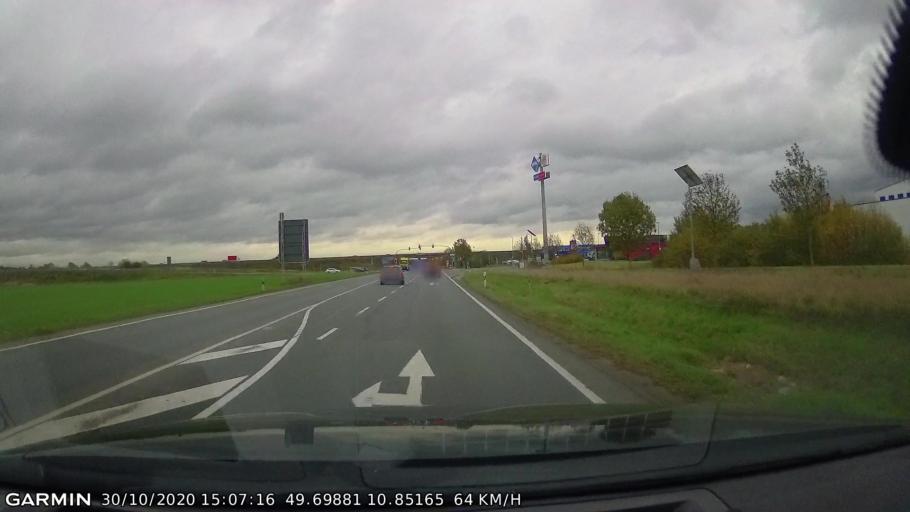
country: DE
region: Bavaria
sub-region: Regierungsbezirk Mittelfranken
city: Gremsdorf
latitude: 49.6988
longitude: 10.8517
